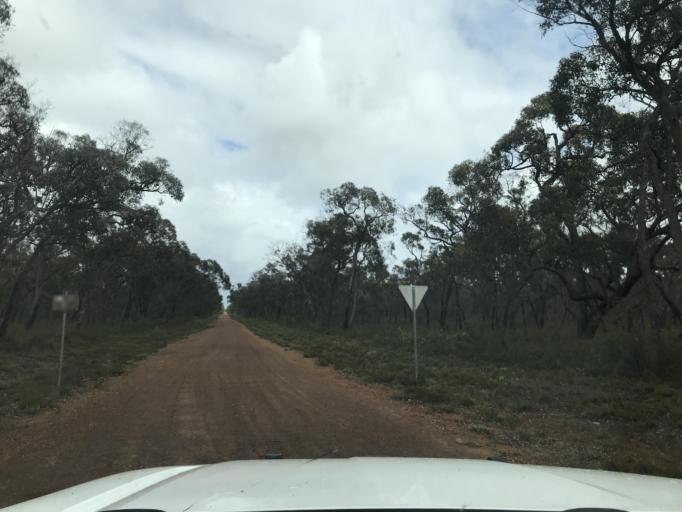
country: AU
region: South Australia
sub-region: Wattle Range
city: Penola
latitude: -37.2957
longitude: 141.3228
